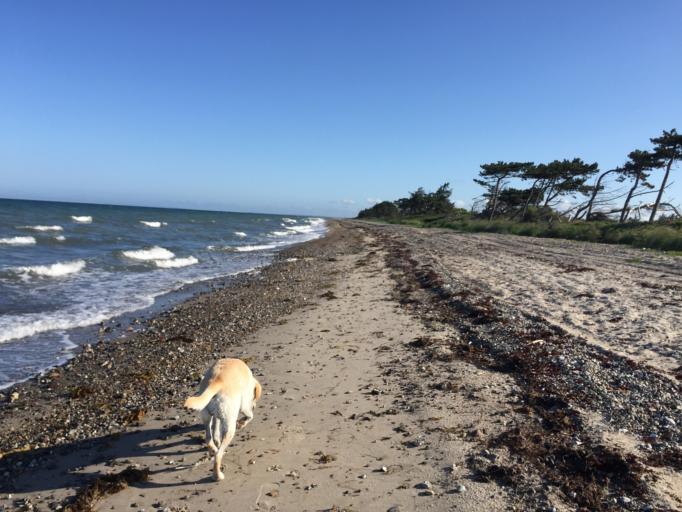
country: DK
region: Zealand
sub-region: Slagelse Kommune
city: Korsor
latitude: 55.2088
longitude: 11.1730
